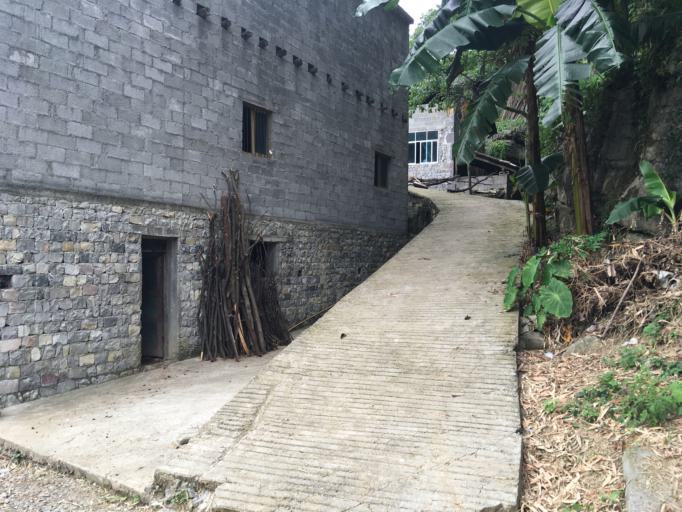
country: CN
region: Guangxi Zhuangzu Zizhiqu
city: Xinzhou
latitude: 25.0551
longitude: 105.7938
